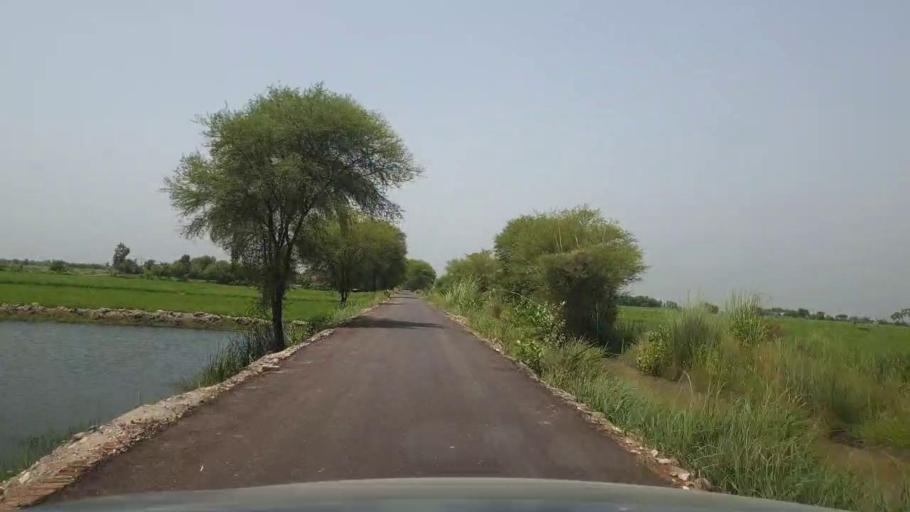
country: PK
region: Sindh
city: Garhi Yasin
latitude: 27.9325
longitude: 68.4306
